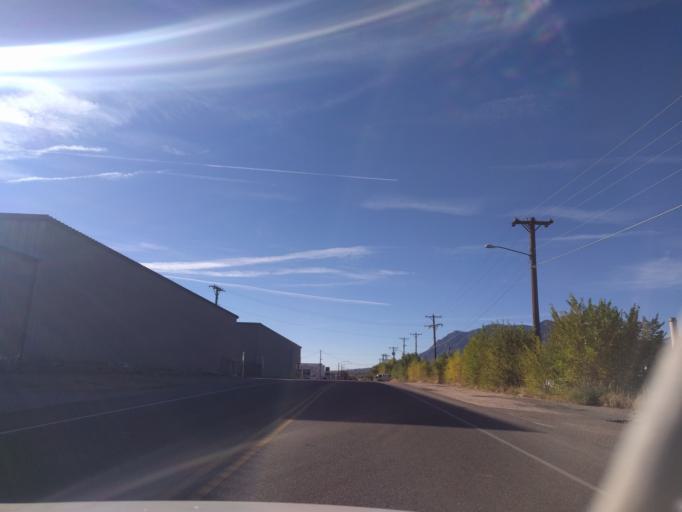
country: US
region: Colorado
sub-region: El Paso County
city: Colorado Springs
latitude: 38.8298
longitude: -104.8292
